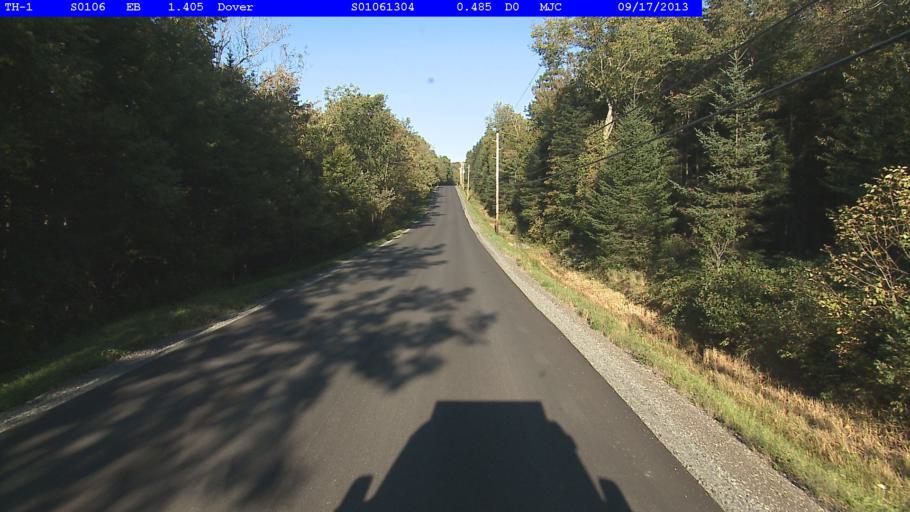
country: US
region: Vermont
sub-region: Windham County
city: Dover
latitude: 42.9271
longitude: -72.8253
